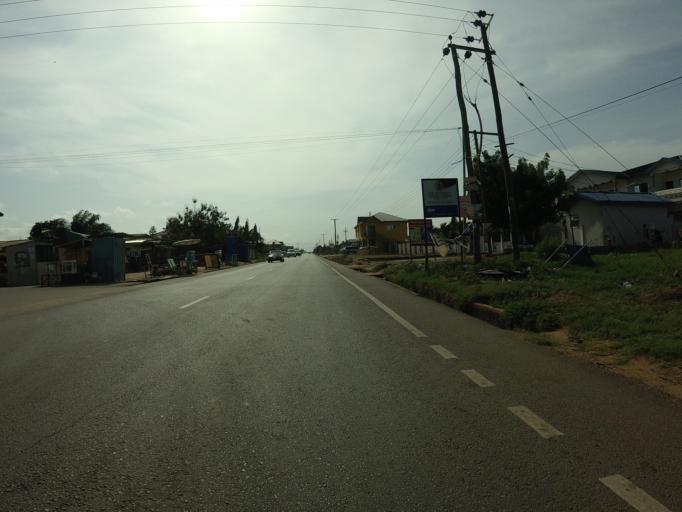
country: GH
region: Greater Accra
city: Nungua
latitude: 5.6451
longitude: -0.0874
